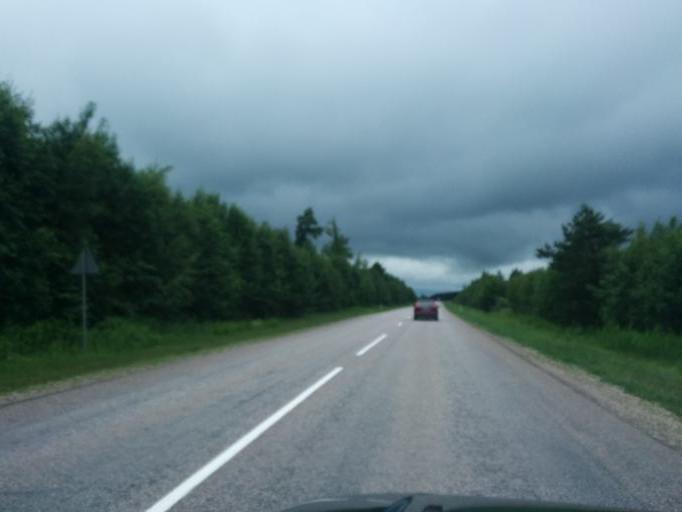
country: LV
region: Beverina
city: Murmuiza
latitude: 57.4817
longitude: 25.6127
